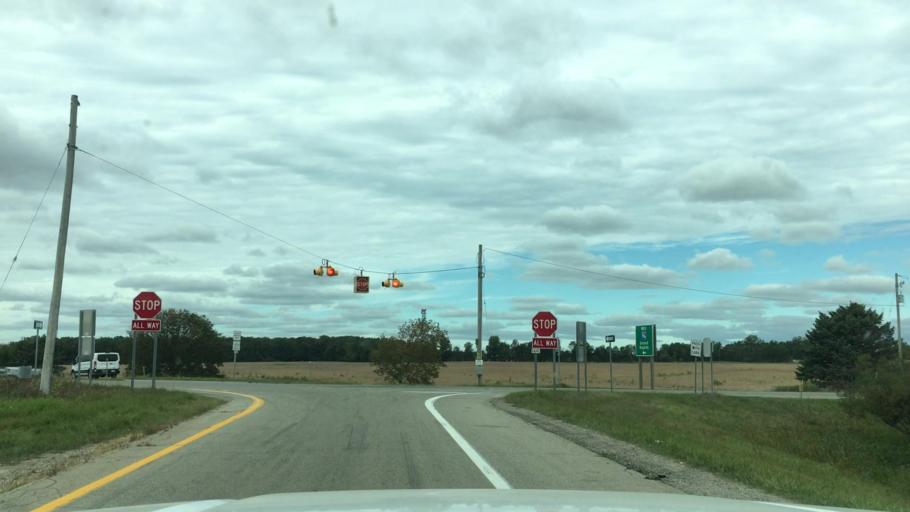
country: US
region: Michigan
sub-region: Ionia County
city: Saranac
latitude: 42.8800
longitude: -85.1337
